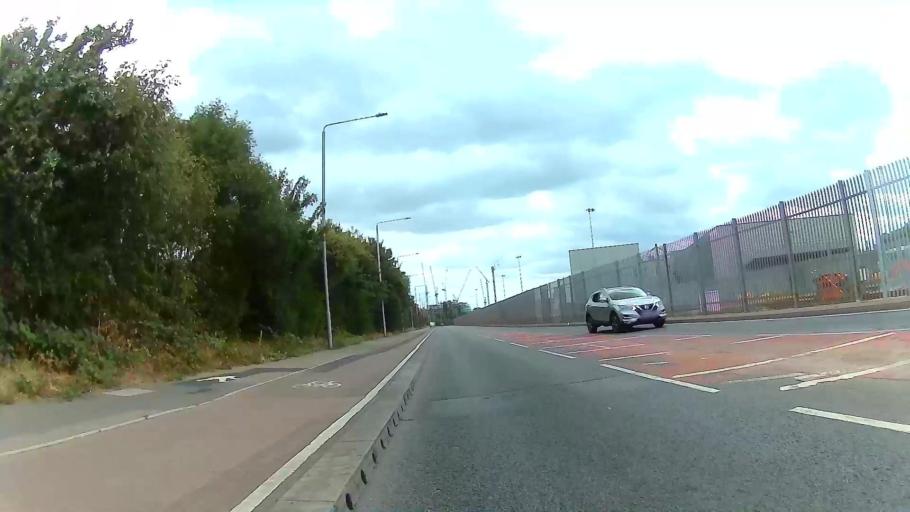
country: GB
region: England
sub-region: Greater London
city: Hackney
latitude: 51.5624
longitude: -0.0271
